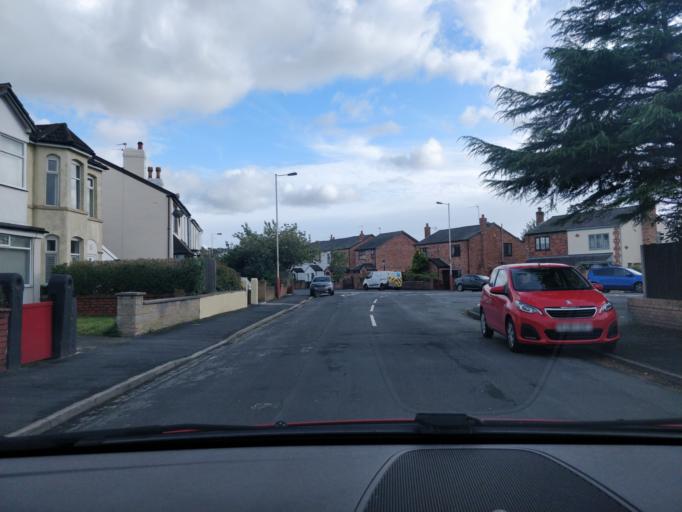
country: GB
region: England
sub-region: Sefton
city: Southport
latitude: 53.6210
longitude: -3.0166
